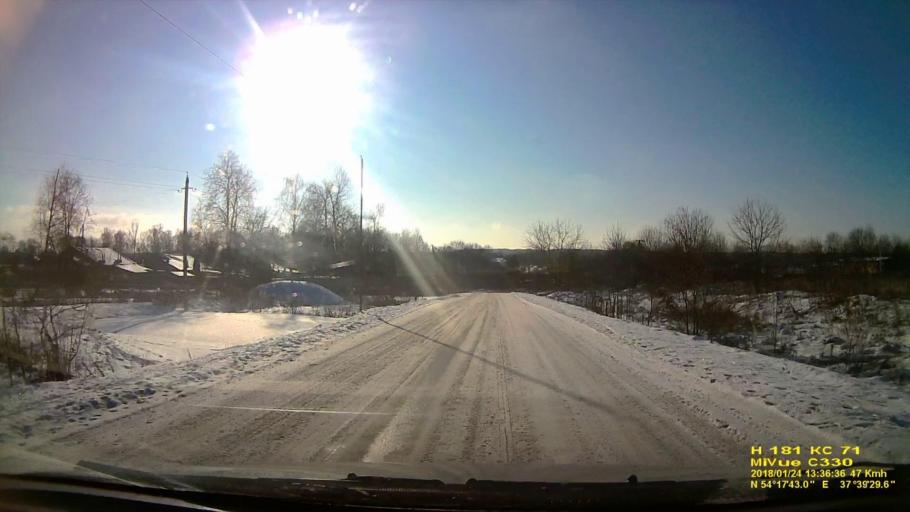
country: RU
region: Tula
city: Gorelki
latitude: 54.2952
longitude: 37.6582
